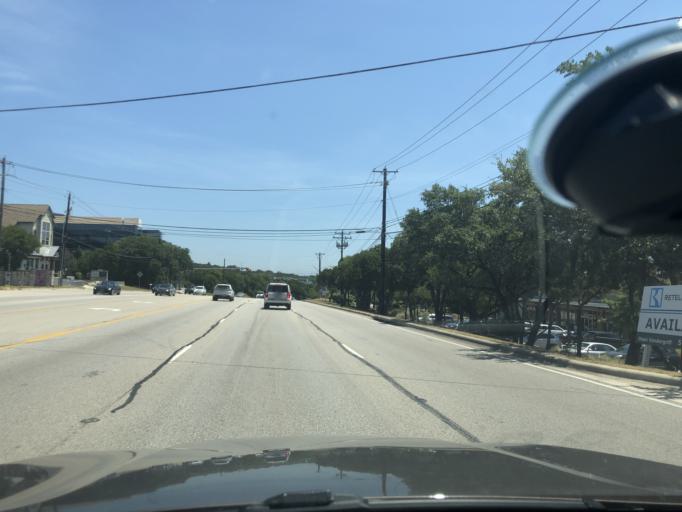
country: US
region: Texas
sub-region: Travis County
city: Lost Creek
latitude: 30.2966
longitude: -97.8339
